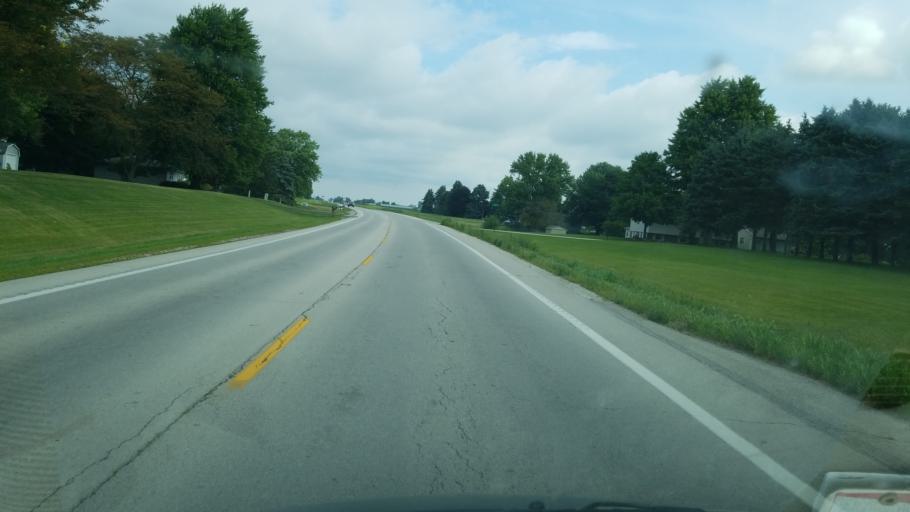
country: US
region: Ohio
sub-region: Sandusky County
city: Ballville
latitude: 41.2967
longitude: -83.1687
